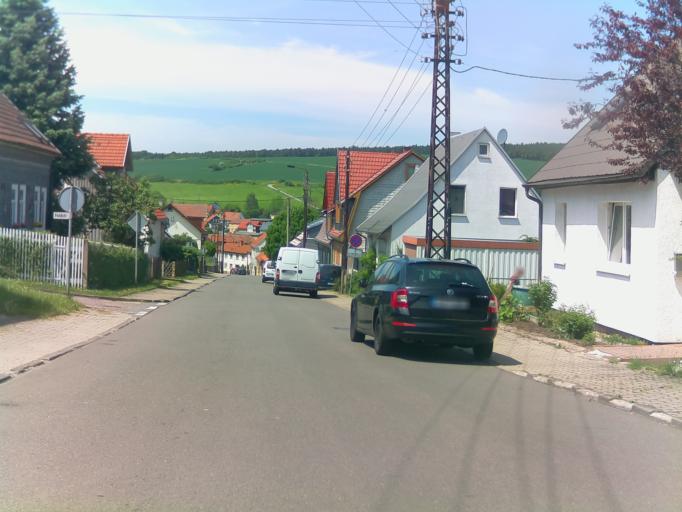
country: DE
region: Thuringia
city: Martinroda
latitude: 50.7222
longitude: 10.8930
